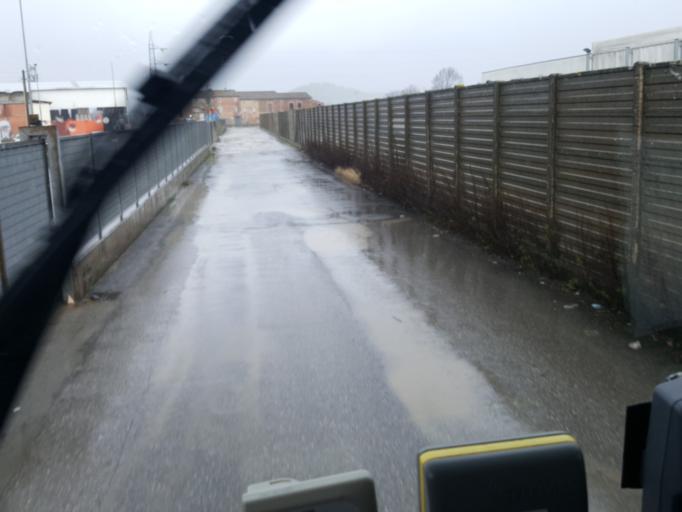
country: IT
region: Tuscany
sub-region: Provincia di Lucca
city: Porcari
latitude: 43.8227
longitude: 10.6120
